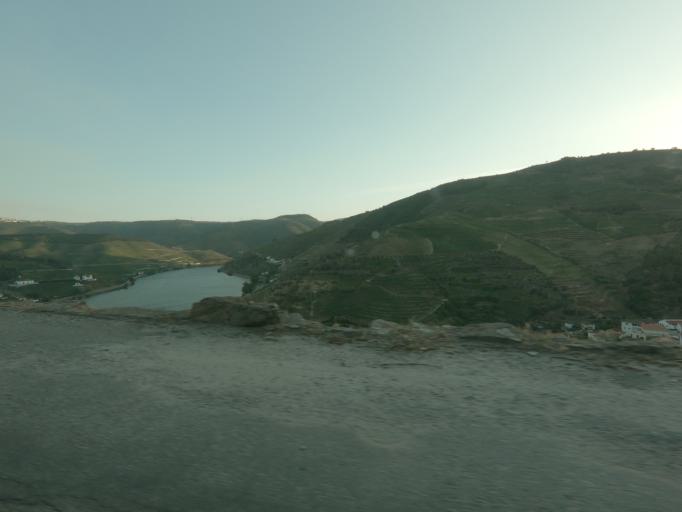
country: PT
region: Viseu
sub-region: Armamar
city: Armamar
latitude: 41.1593
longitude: -7.6807
